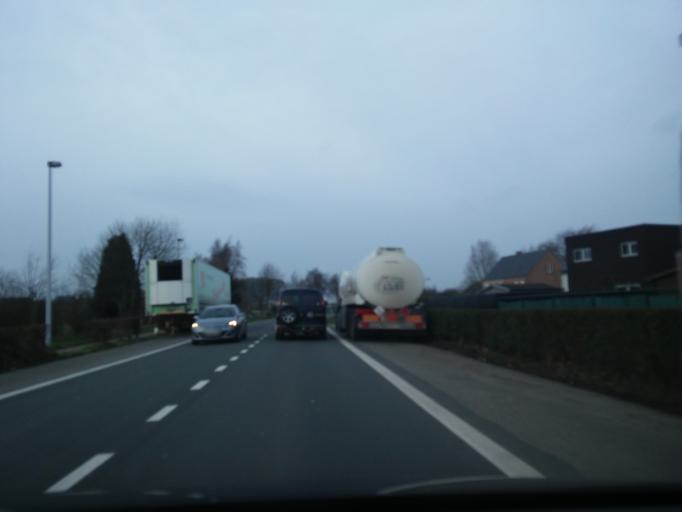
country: BE
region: Flanders
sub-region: Provincie Antwerpen
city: Herselt
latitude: 51.0888
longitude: 4.8690
